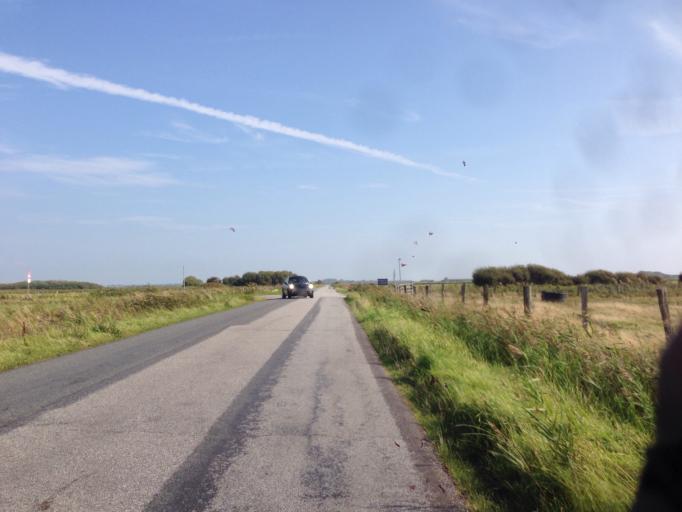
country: DE
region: Schleswig-Holstein
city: Tinnum
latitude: 54.8842
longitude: 8.3481
